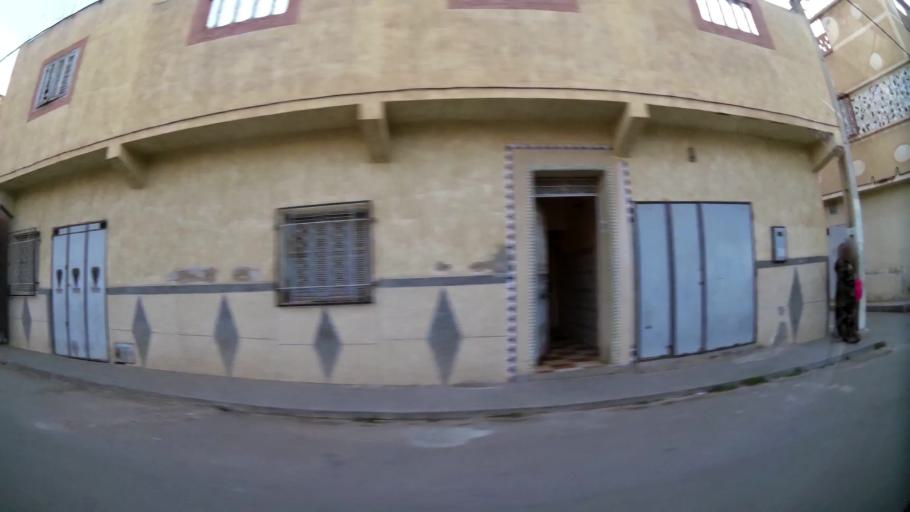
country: MA
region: Oriental
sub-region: Oujda-Angad
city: Oujda
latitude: 34.6827
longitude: -1.8810
